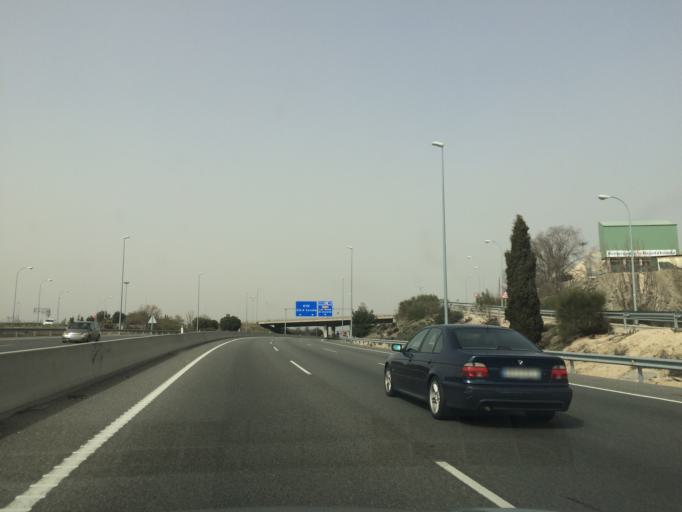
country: ES
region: Madrid
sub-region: Provincia de Madrid
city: Majadahonda
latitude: 40.4765
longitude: -3.8957
